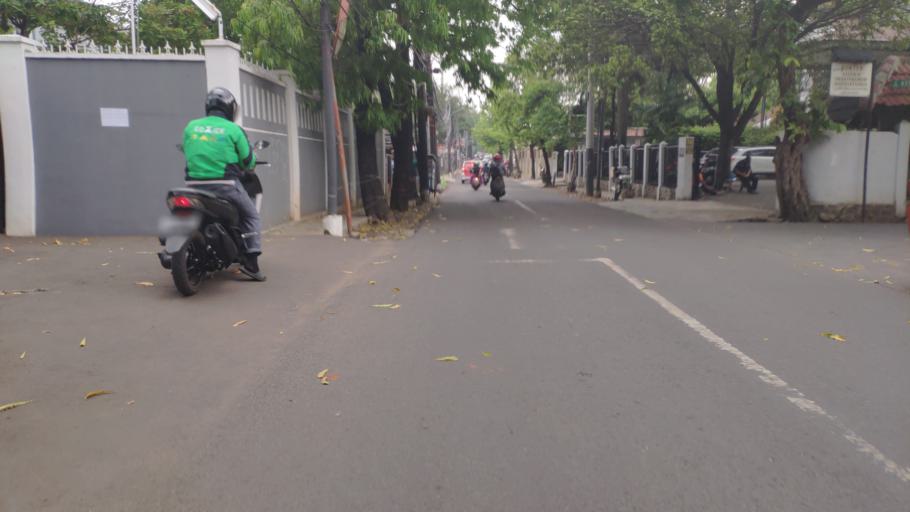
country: ID
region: Jakarta Raya
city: Jakarta
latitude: -6.2721
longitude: 106.8216
